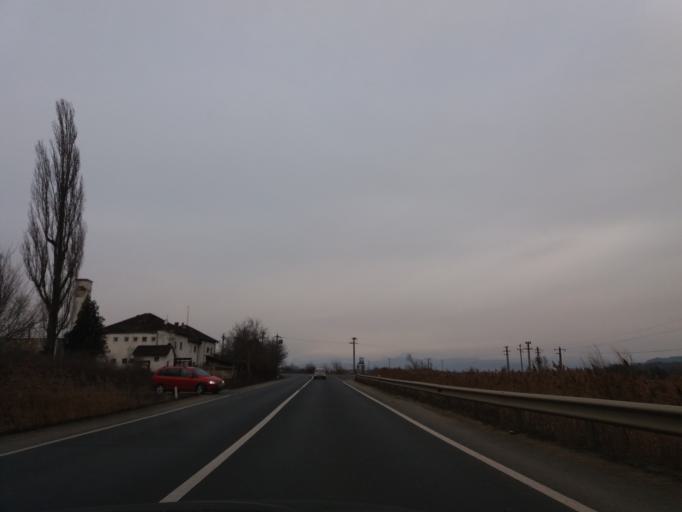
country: RO
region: Hunedoara
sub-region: Comuna Calan
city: Calan
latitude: 45.7583
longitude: 23.0009
